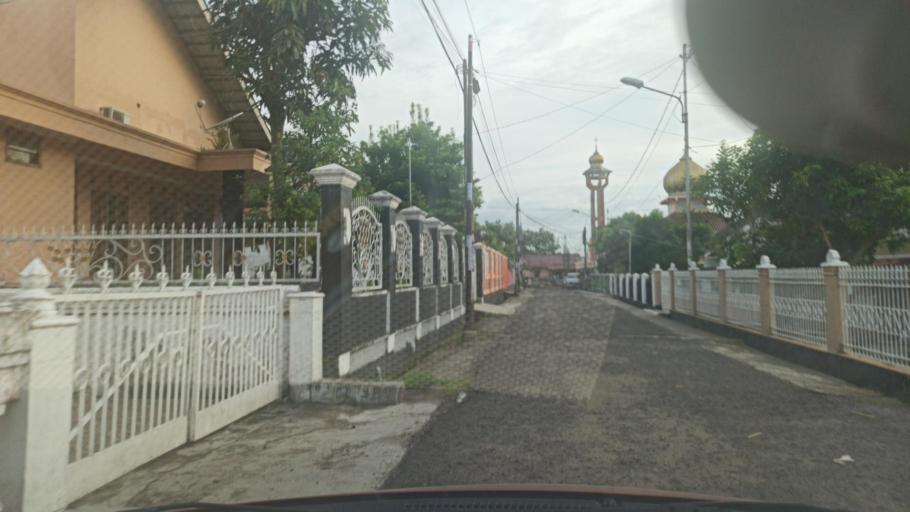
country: ID
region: South Sumatra
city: Palembang
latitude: -2.9613
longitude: 104.7302
